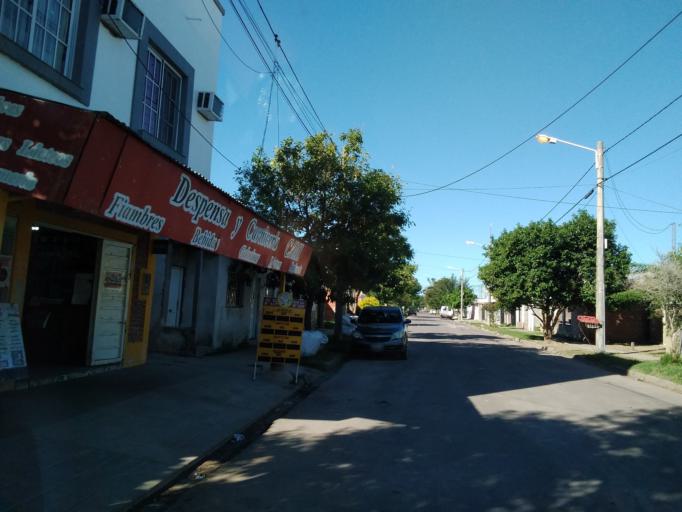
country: AR
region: Corrientes
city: Corrientes
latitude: -27.4579
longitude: -58.7699
